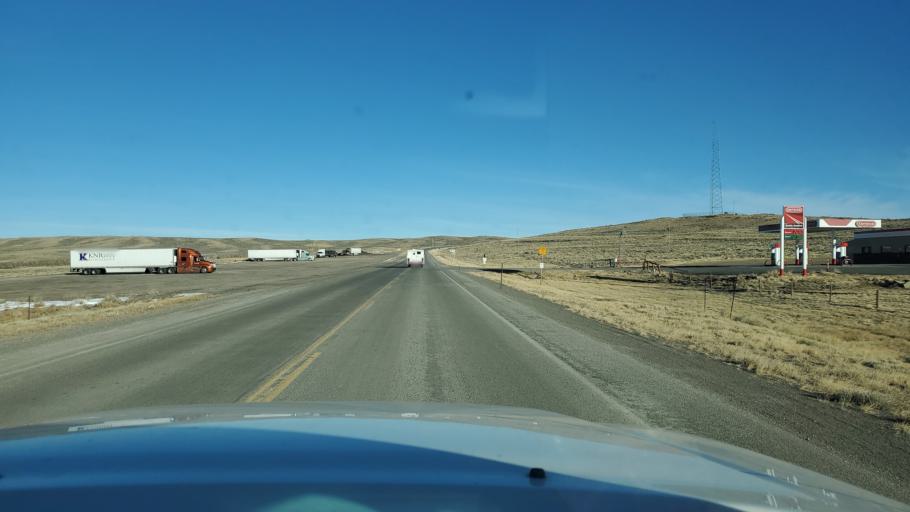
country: US
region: Wyoming
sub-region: Carbon County
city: Saratoga
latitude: 41.7265
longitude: -106.4598
